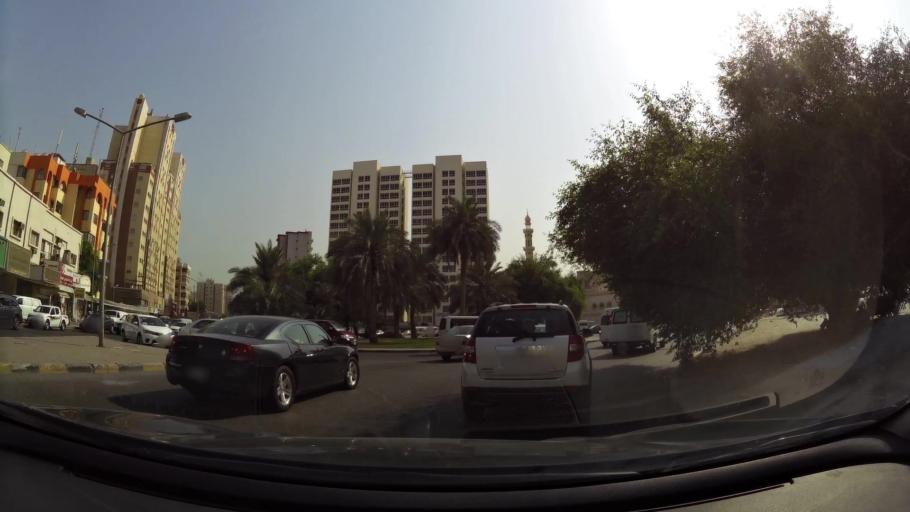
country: KW
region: Muhafazat Hawalli
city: As Salimiyah
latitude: 29.3268
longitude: 48.0568
